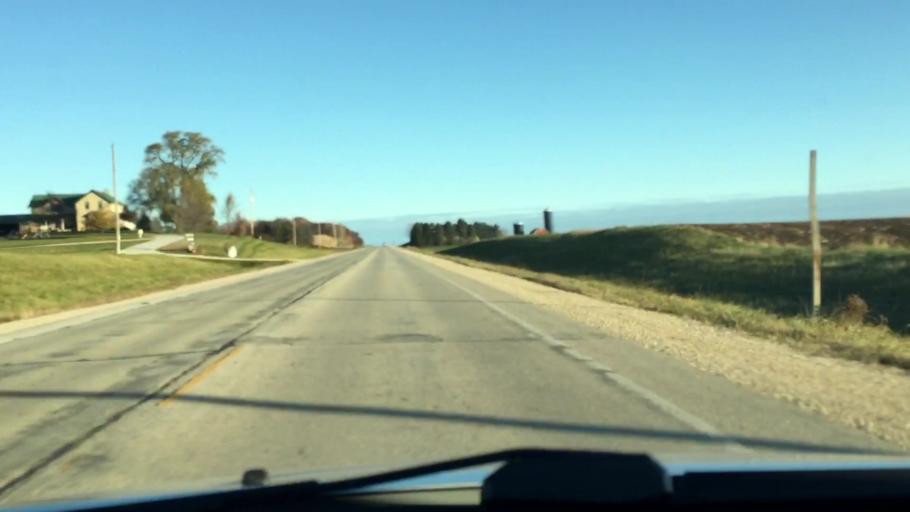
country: US
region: Wisconsin
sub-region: Washington County
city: Hartford
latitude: 43.3998
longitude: -88.4602
